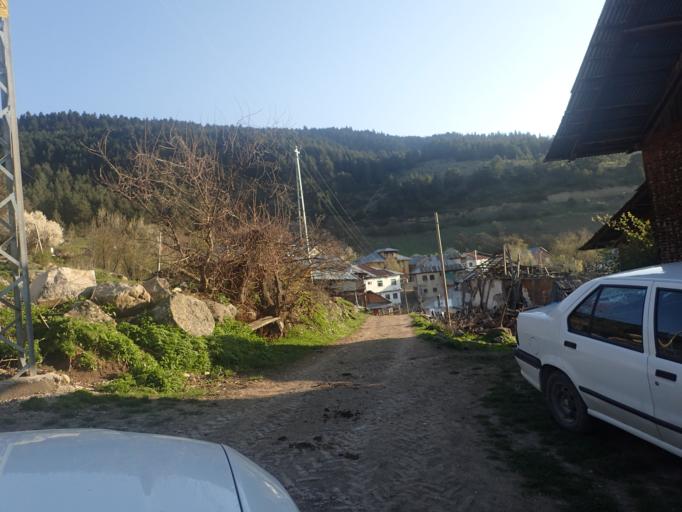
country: TR
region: Sivas
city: Koyulhisar
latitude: 40.3580
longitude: 37.8529
